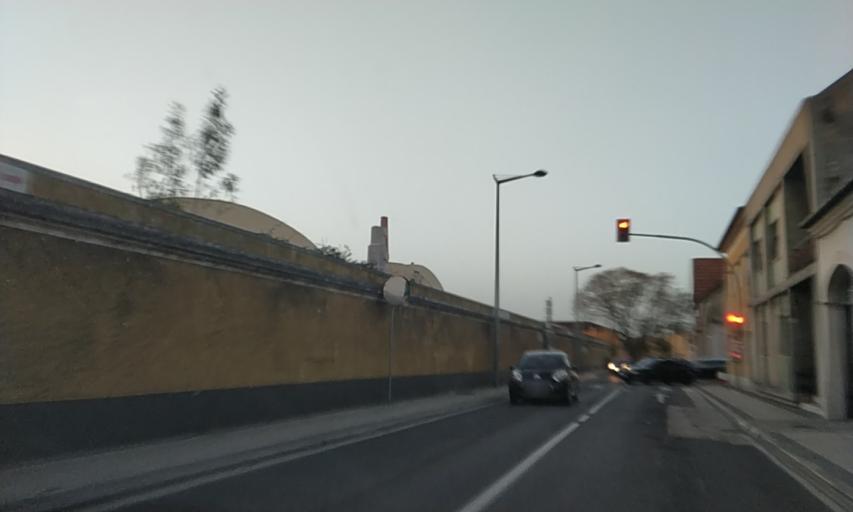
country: PT
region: Leiria
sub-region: Marinha Grande
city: Marinha Grande
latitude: 39.7503
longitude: -8.9333
